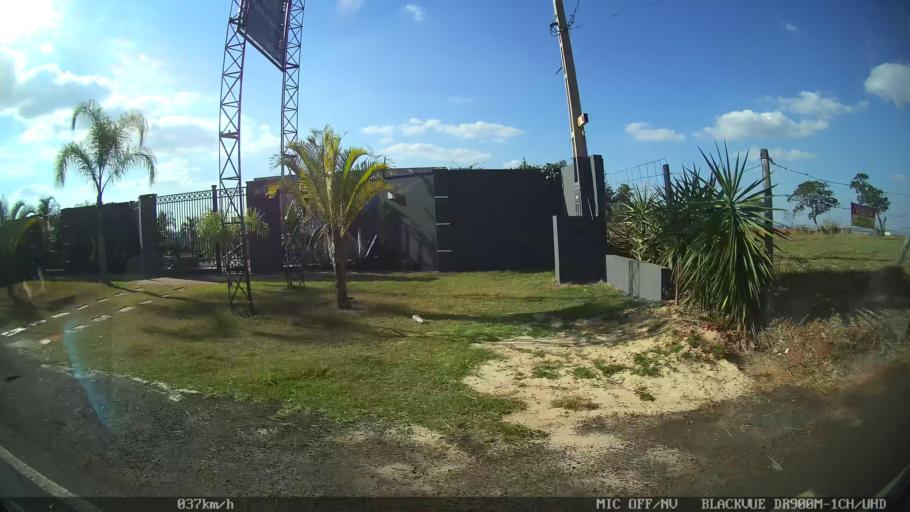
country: BR
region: Sao Paulo
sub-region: Nova Odessa
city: Nova Odessa
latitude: -22.8135
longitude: -47.3262
